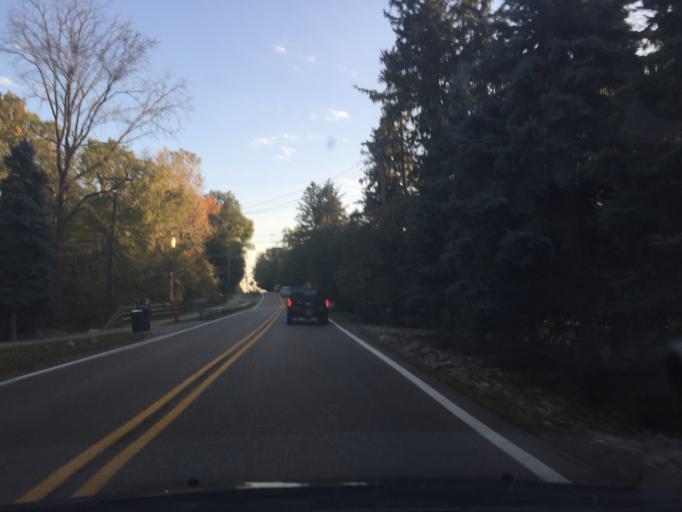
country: US
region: Michigan
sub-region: Oakland County
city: Bloomfield Hills
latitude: 42.5840
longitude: -83.2867
